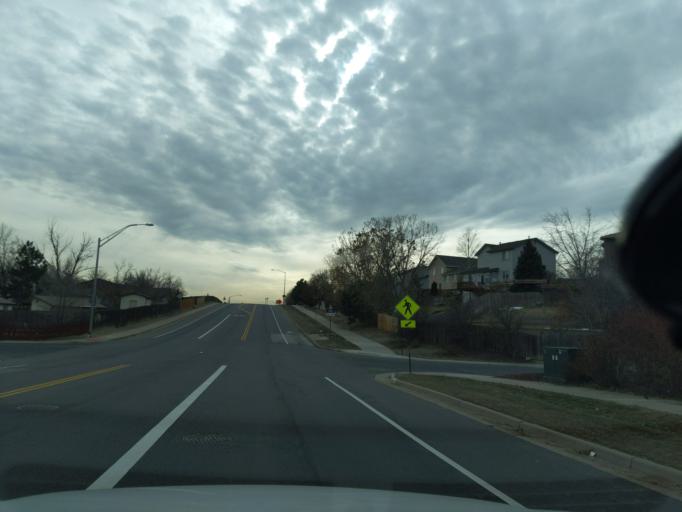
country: US
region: Colorado
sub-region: Adams County
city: Thornton
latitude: 39.8732
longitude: -104.9590
